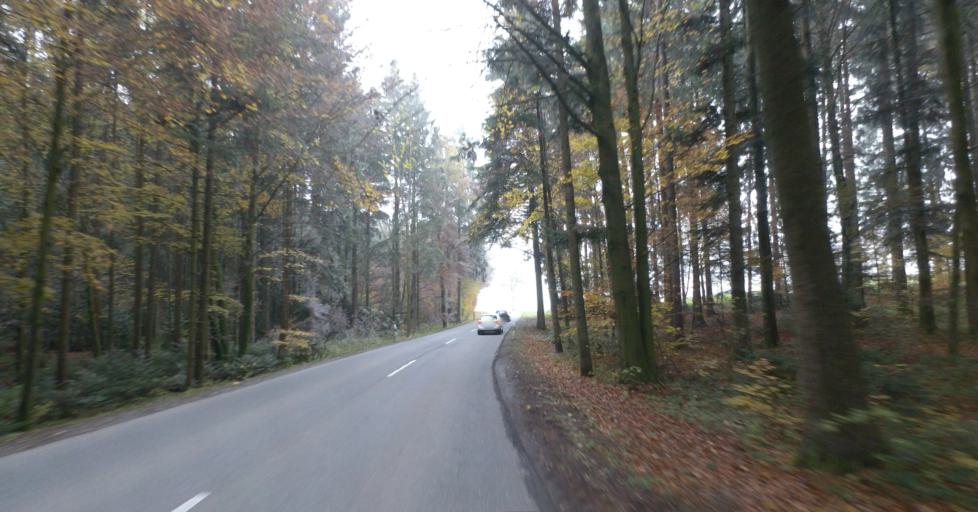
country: DE
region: Bavaria
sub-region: Upper Bavaria
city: Seeon-Seebruck
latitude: 47.9708
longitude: 12.5228
